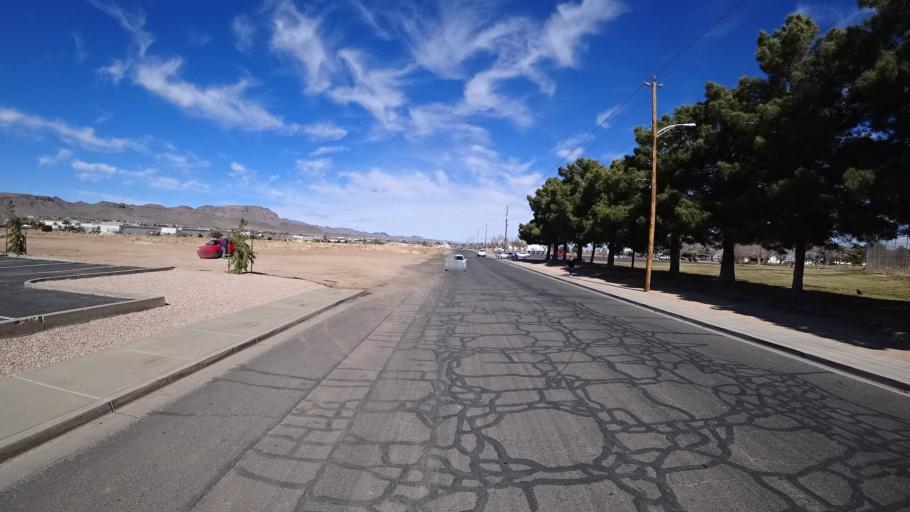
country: US
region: Arizona
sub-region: Mohave County
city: Kingman
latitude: 35.2196
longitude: -114.0292
